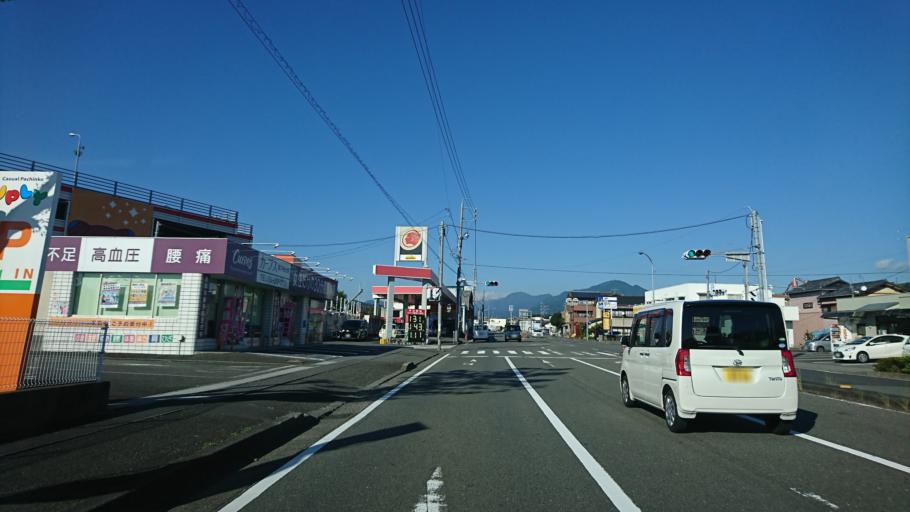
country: JP
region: Shizuoka
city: Shizuoka-shi
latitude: 34.9951
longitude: 138.3643
